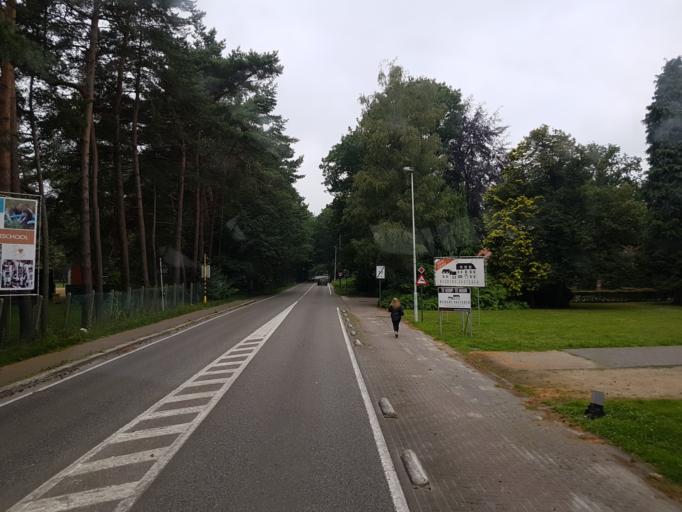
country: BE
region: Flanders
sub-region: Provincie Antwerpen
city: Schoten
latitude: 51.2666
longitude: 4.5389
